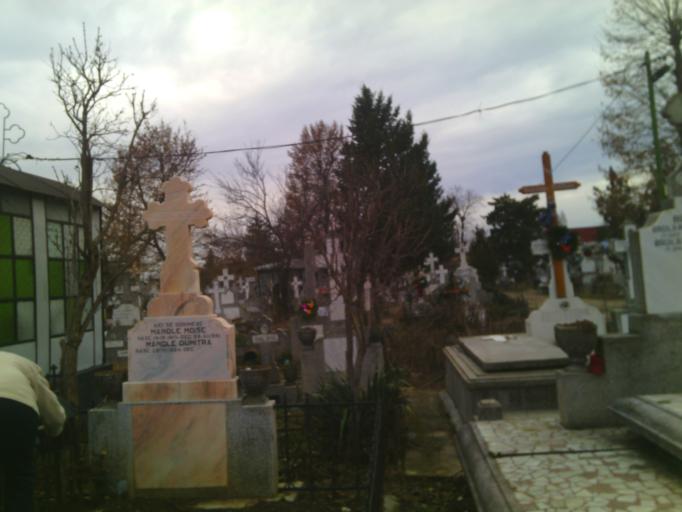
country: RO
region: Ilfov
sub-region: Comuna Jilava
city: Jilava
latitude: 44.3796
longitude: 26.0827
